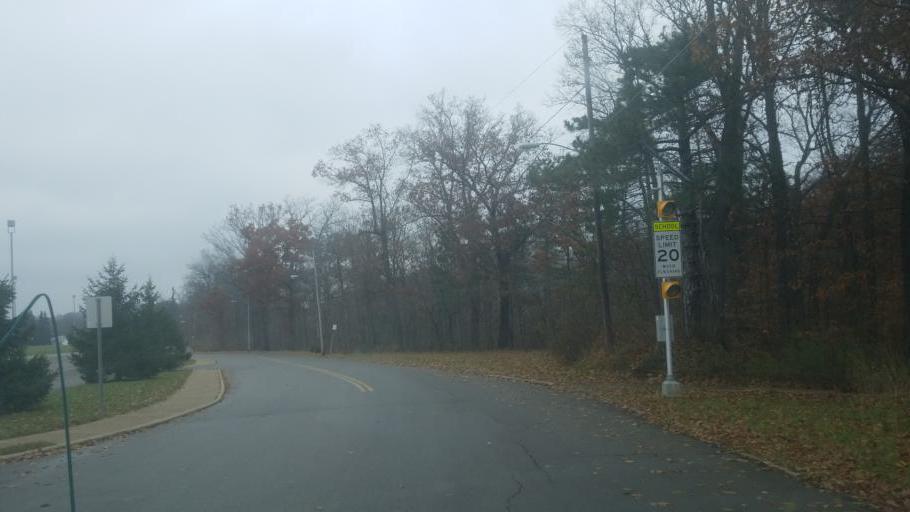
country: US
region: Ohio
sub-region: Richland County
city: Mansfield
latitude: 40.7610
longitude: -82.5413
